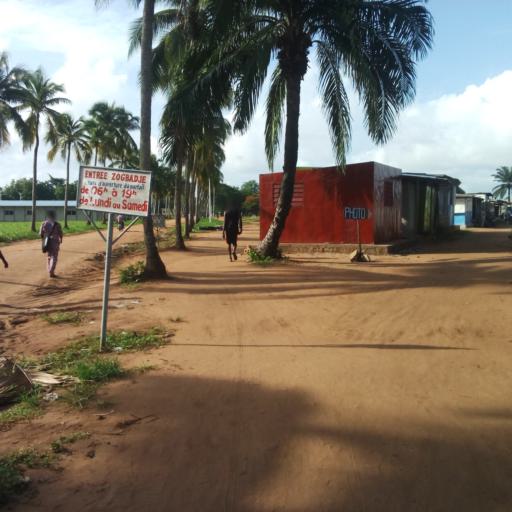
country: BJ
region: Atlantique
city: Abomey-Calavi
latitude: 6.4226
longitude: 2.3391
